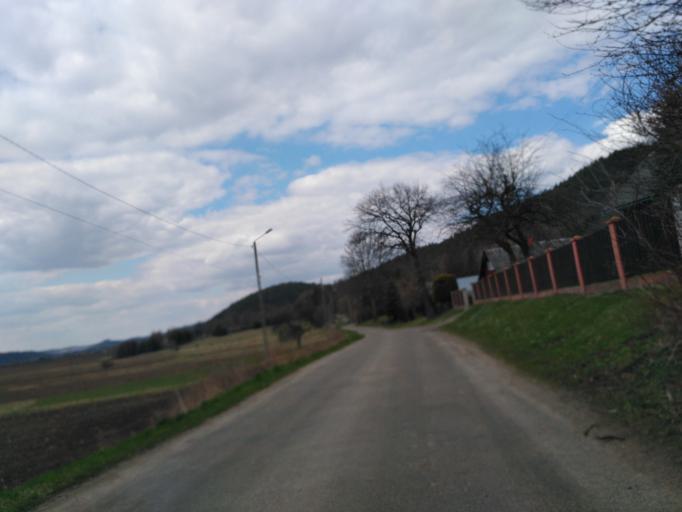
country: PL
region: Subcarpathian Voivodeship
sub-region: Powiat brzozowski
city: Dydnia
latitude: 49.6657
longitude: 22.2895
